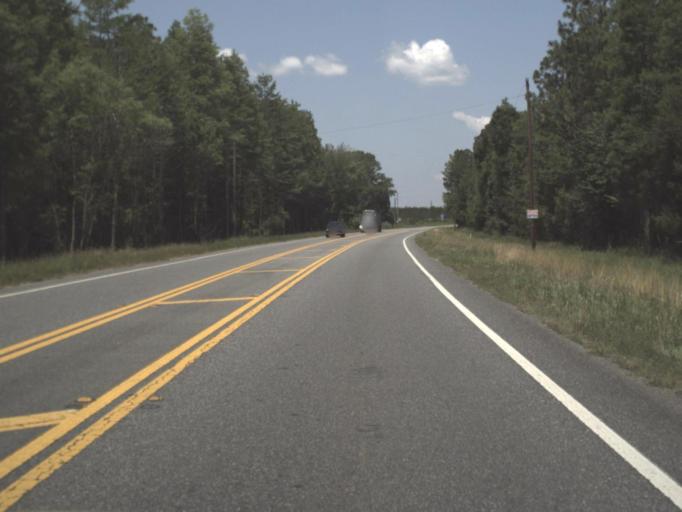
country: US
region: Florida
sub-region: Bradford County
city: Starke
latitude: 29.9448
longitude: -82.1337
